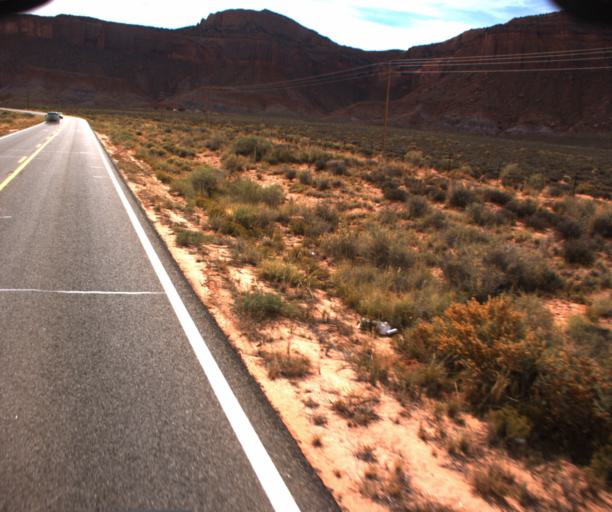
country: US
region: Arizona
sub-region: Navajo County
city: Kayenta
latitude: 36.8505
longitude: -110.2709
